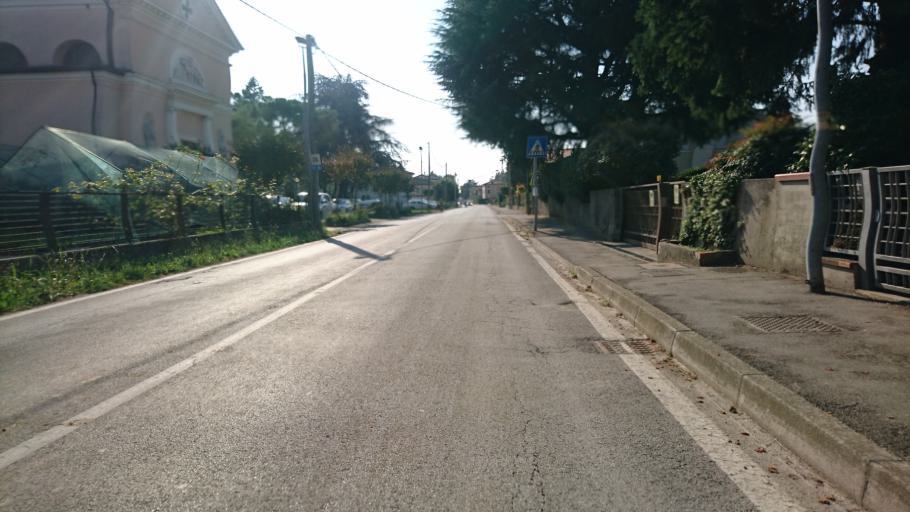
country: IT
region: Veneto
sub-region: Provincia di Padova
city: Gazzo
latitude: 45.5843
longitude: 11.7053
